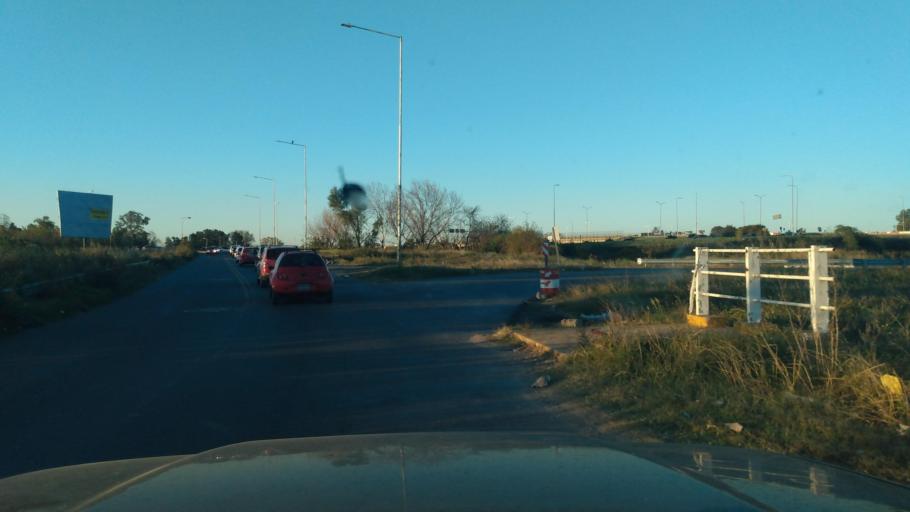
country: AR
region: Buenos Aires
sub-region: Partido de Merlo
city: Merlo
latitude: -34.6301
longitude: -58.7245
